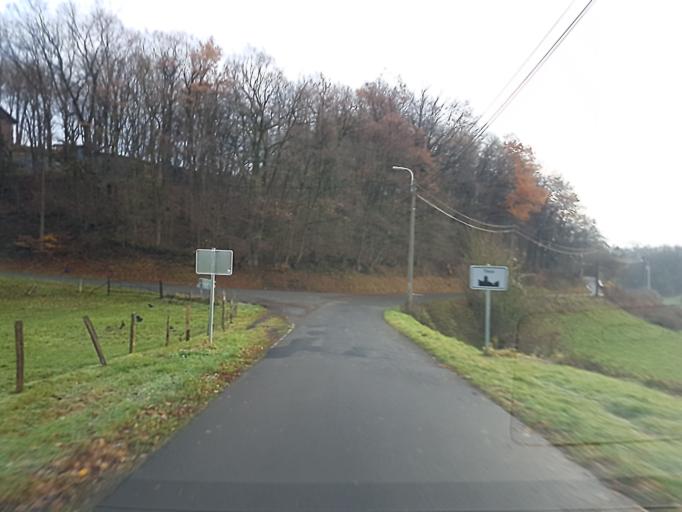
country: BE
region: Wallonia
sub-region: Province de Liege
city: Theux
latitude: 50.5444
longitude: 5.7936
